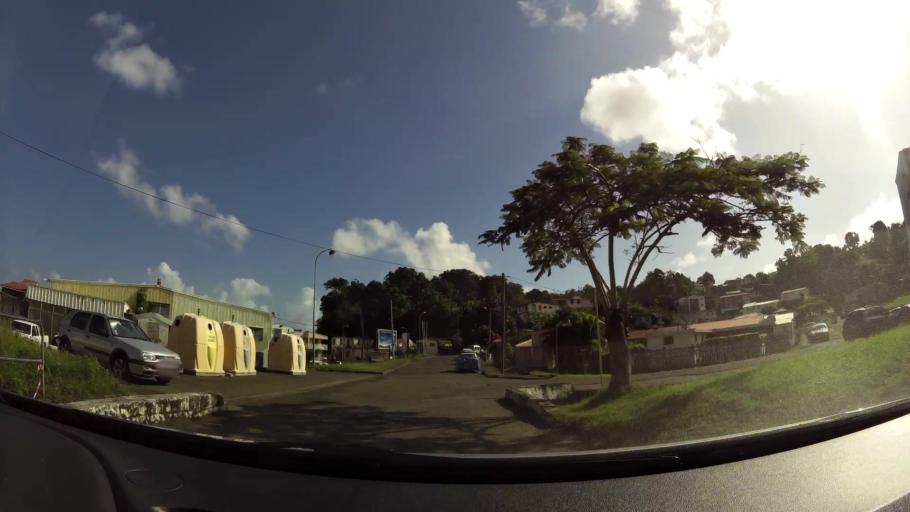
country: MQ
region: Martinique
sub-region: Martinique
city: La Trinite
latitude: 14.7360
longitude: -60.9624
